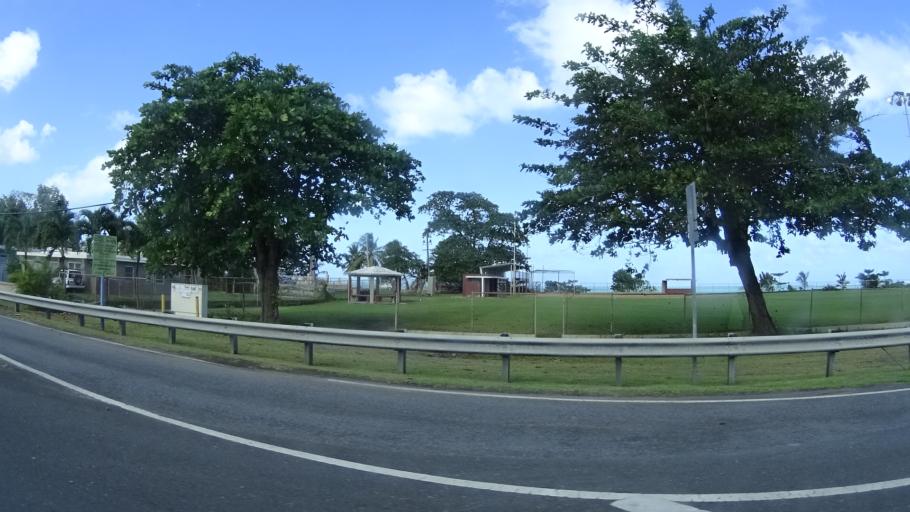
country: PR
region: Luquillo
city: Playa Fortuna
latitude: 18.3792
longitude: -65.7408
